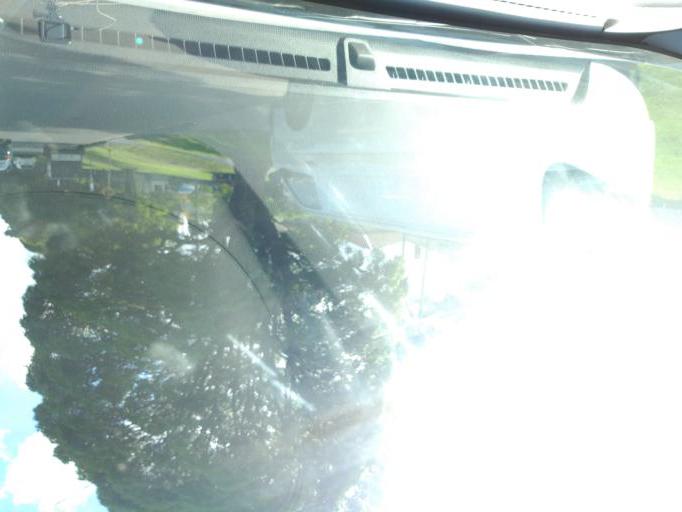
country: AU
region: New South Wales
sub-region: Wollongong
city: Helensburgh
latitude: -34.1942
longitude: 150.9814
